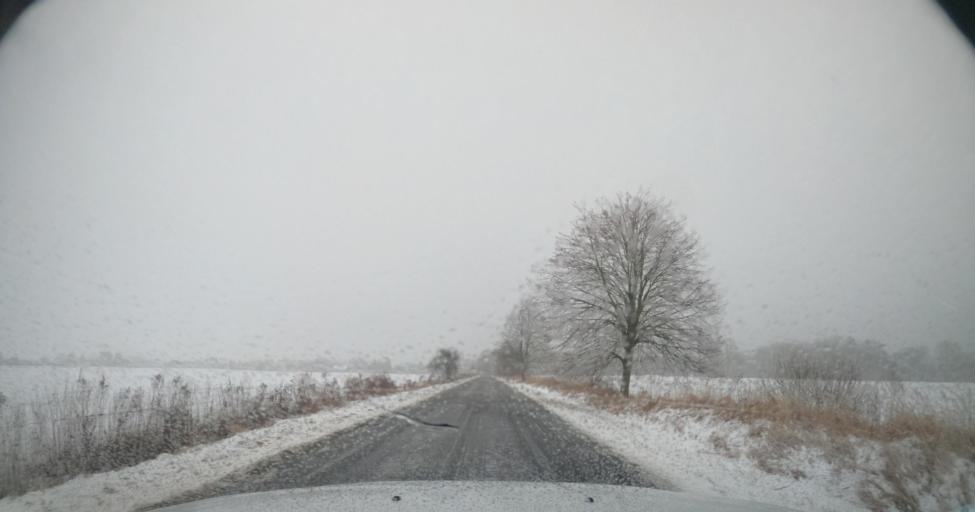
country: PL
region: West Pomeranian Voivodeship
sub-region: Powiat kamienski
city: Golczewo
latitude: 53.7632
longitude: 14.9002
